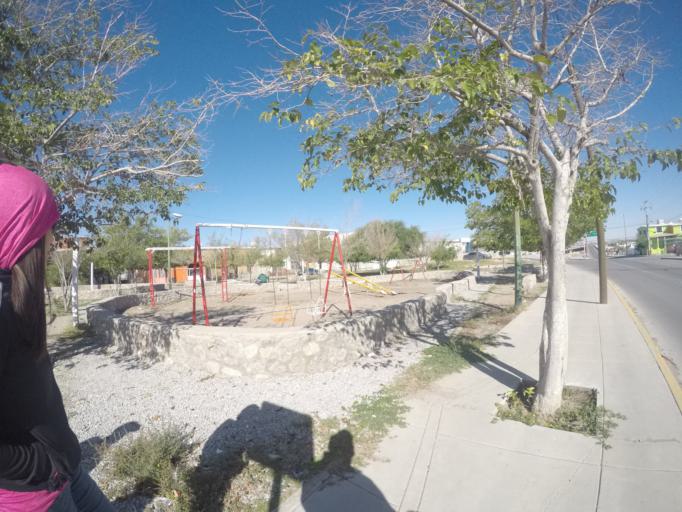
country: US
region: Texas
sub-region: El Paso County
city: Socorro
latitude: 31.6679
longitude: -106.4012
